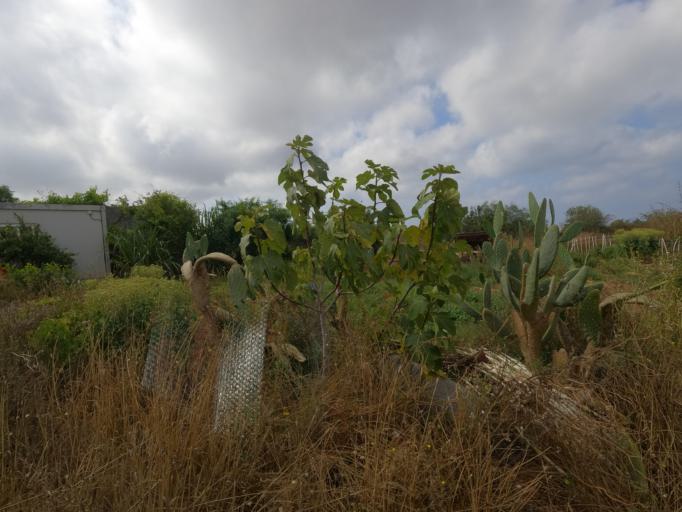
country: CY
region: Ammochostos
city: Ayia Napa
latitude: 34.9993
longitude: 34.0176
